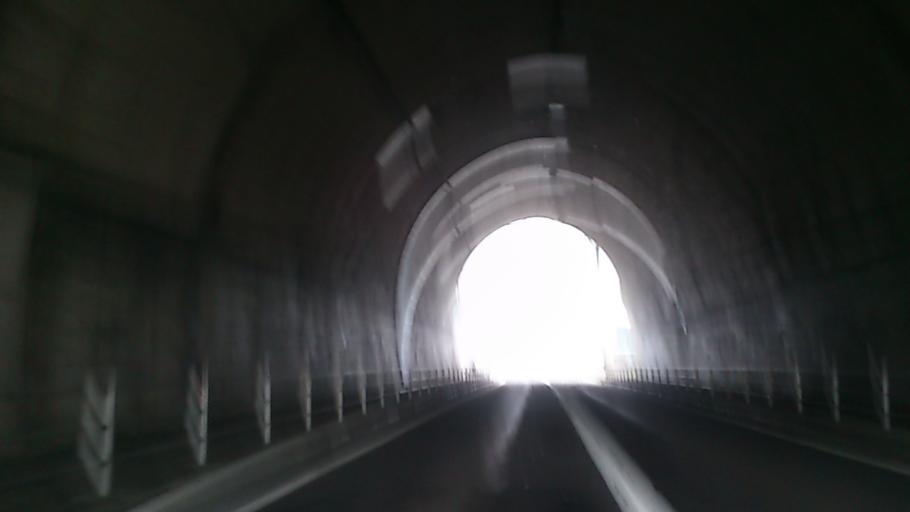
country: JP
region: Hokkaido
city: Iwanai
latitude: 42.4592
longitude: 139.8519
